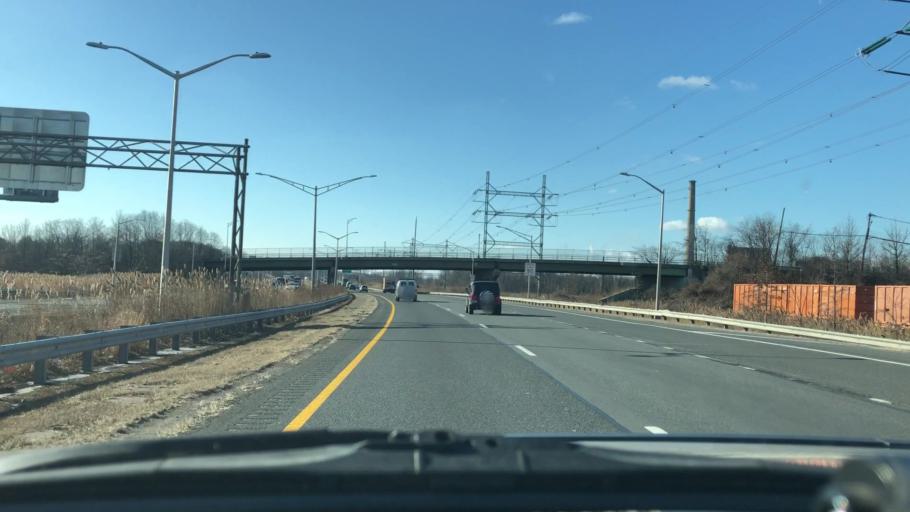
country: US
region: New York
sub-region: Richmond County
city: Bloomfield
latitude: 40.5990
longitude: -74.1907
